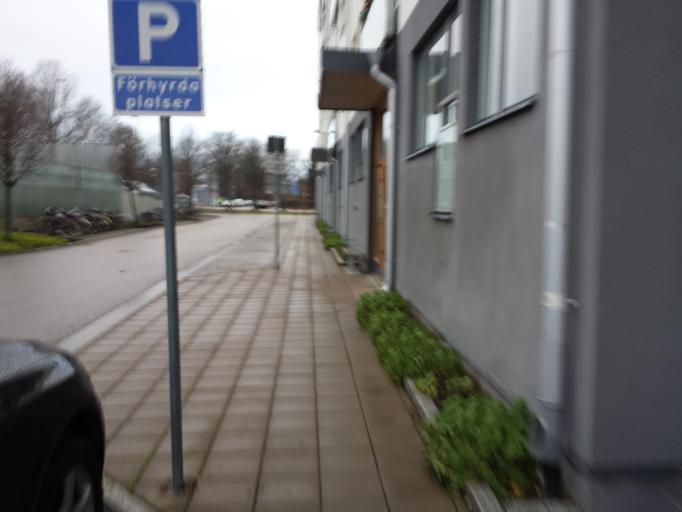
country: SE
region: Uppsala
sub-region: Uppsala Kommun
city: Uppsala
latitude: 59.8669
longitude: 17.6242
